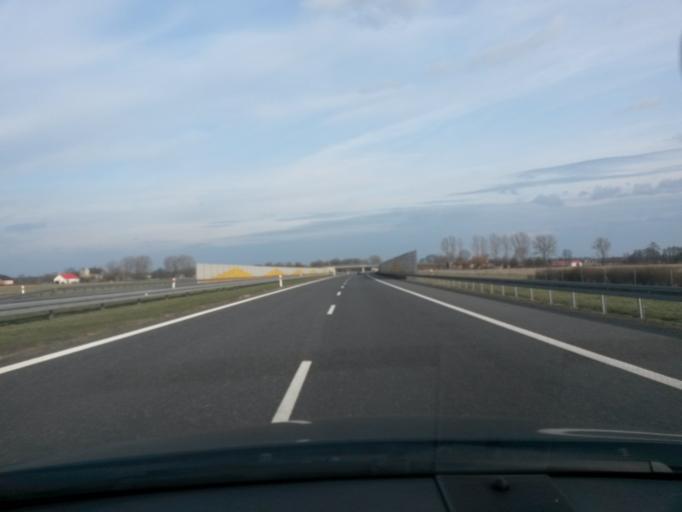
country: PL
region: Lodz Voivodeship
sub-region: Powiat poddebicki
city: Wartkowice
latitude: 52.0117
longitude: 18.9650
